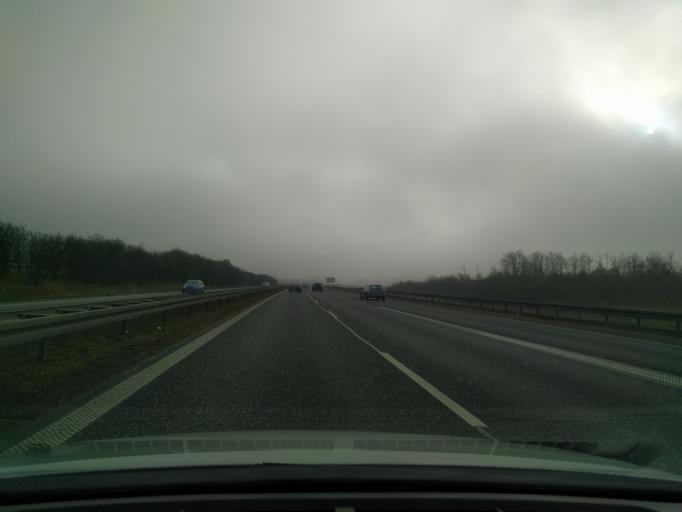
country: DK
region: Zealand
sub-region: Soro Kommune
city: Soro
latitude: 55.4578
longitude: 11.5718
